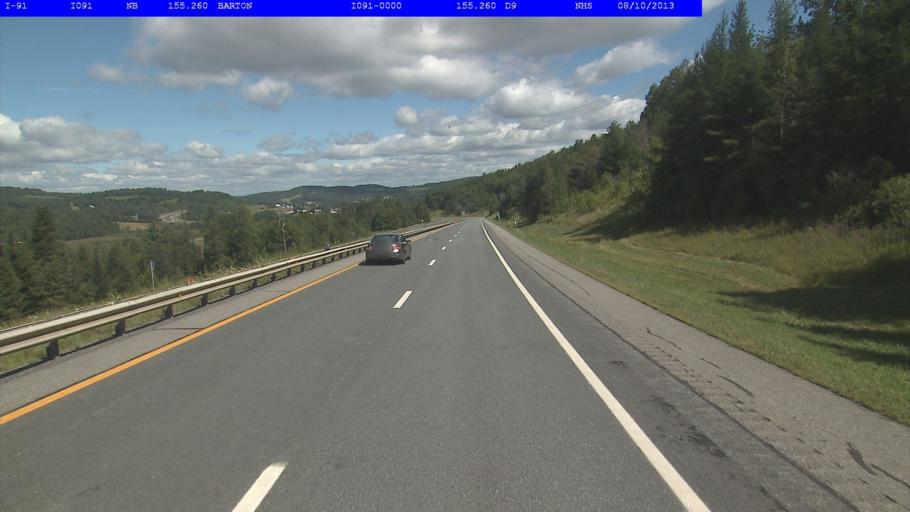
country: US
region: Vermont
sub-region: Orleans County
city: Newport
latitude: 44.7264
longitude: -72.1801
